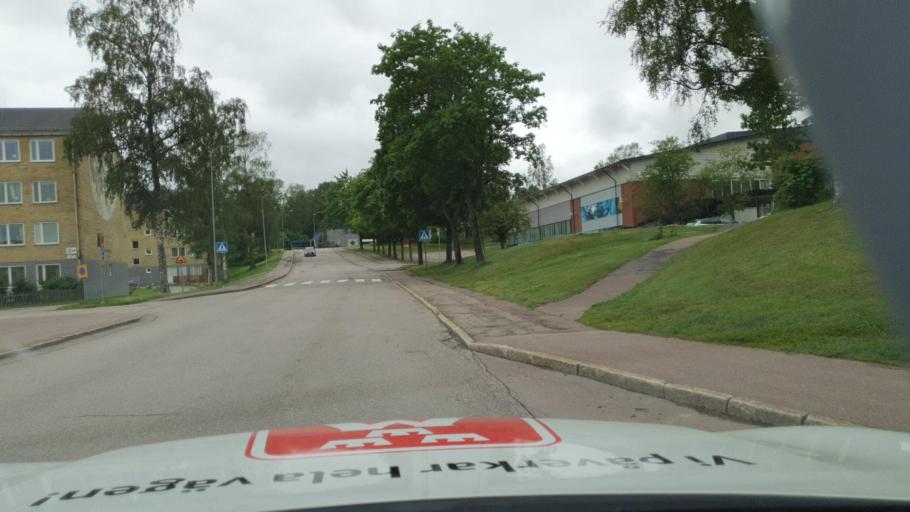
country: SE
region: Vaermland
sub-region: Grums Kommun
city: Grums
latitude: 59.3534
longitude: 13.1074
